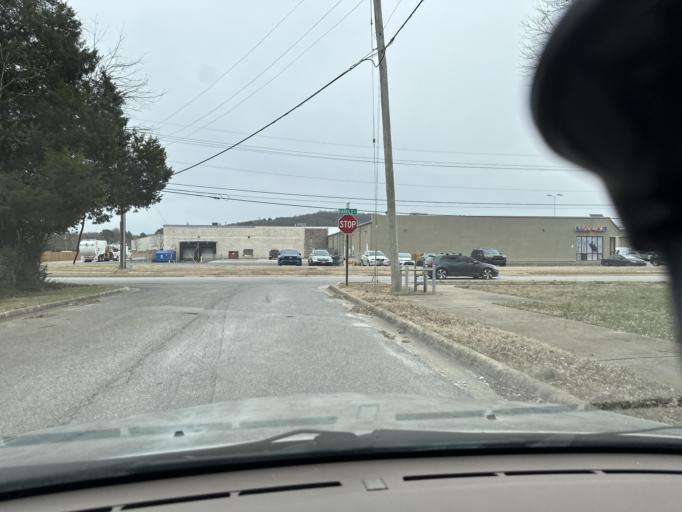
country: US
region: Arkansas
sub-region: Washington County
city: Johnson
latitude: 36.1100
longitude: -94.1434
